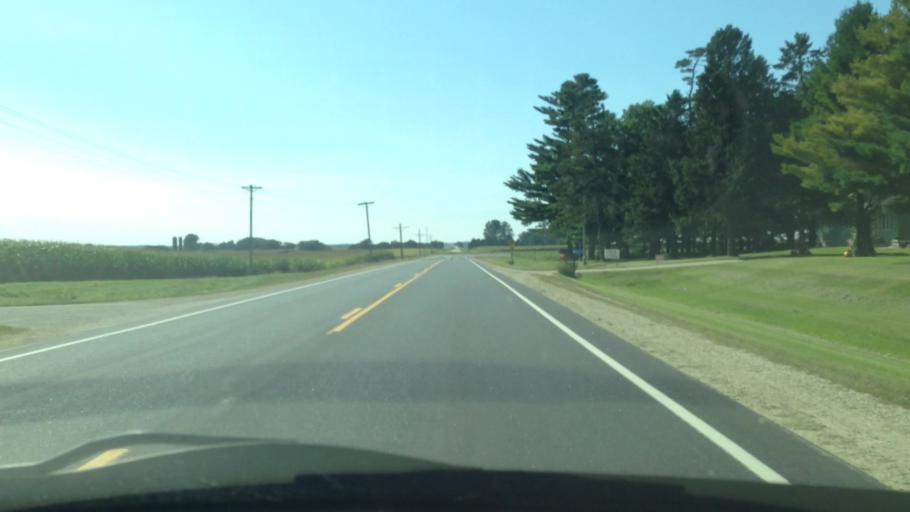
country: US
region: Minnesota
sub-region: Winona County
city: Lewiston
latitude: 43.9697
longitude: -91.8529
